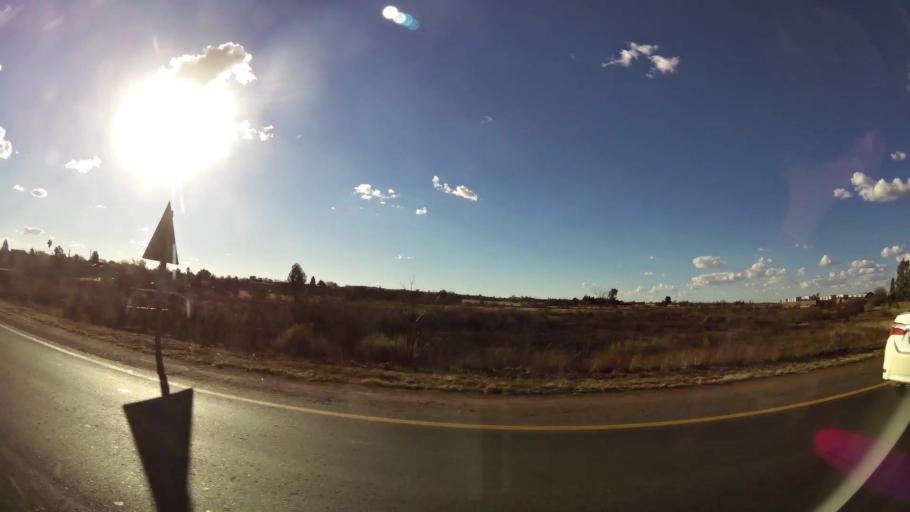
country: ZA
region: North-West
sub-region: Dr Kenneth Kaunda District Municipality
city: Klerksdorp
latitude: -26.8488
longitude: 26.6983
